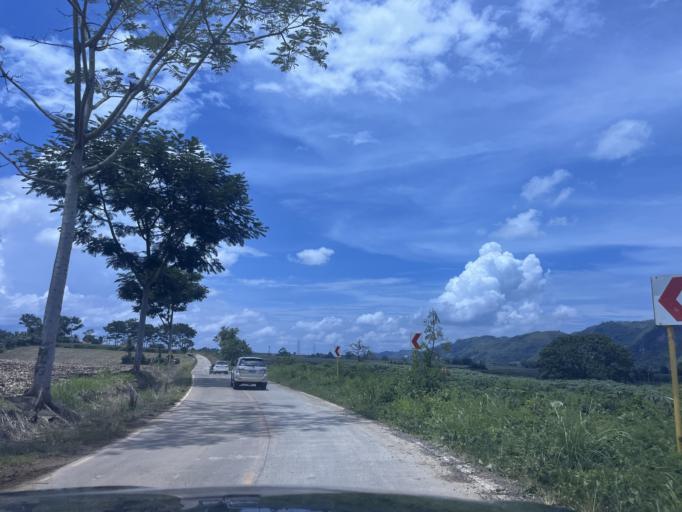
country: PH
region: Northern Mindanao
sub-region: Province of Bukidnon
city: Kisolon
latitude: 8.3121
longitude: 124.9631
